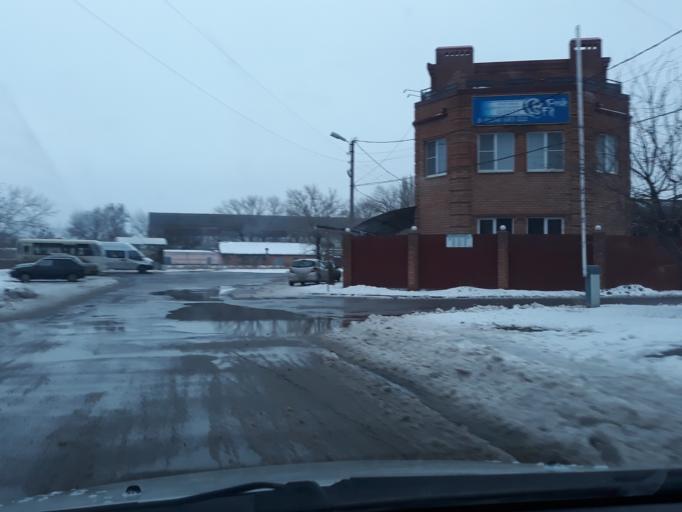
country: RU
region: Rostov
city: Taganrog
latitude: 47.2407
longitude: 38.8673
